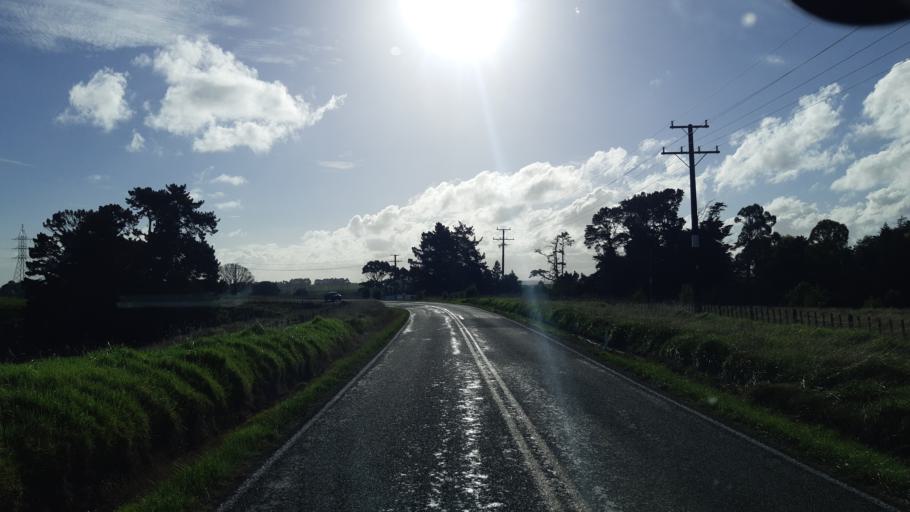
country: NZ
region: Manawatu-Wanganui
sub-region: Wanganui District
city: Wanganui
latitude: -39.9398
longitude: 175.1253
